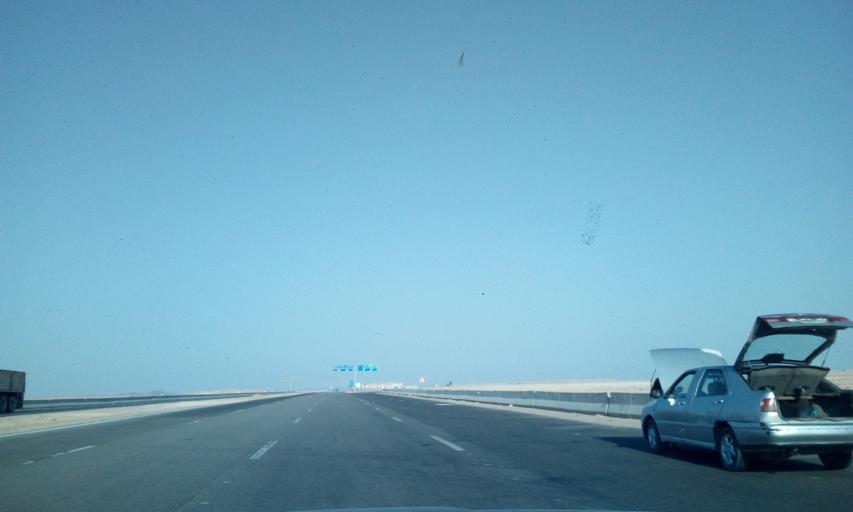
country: EG
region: As Suways
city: Ain Sukhna
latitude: 29.1090
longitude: 32.5341
